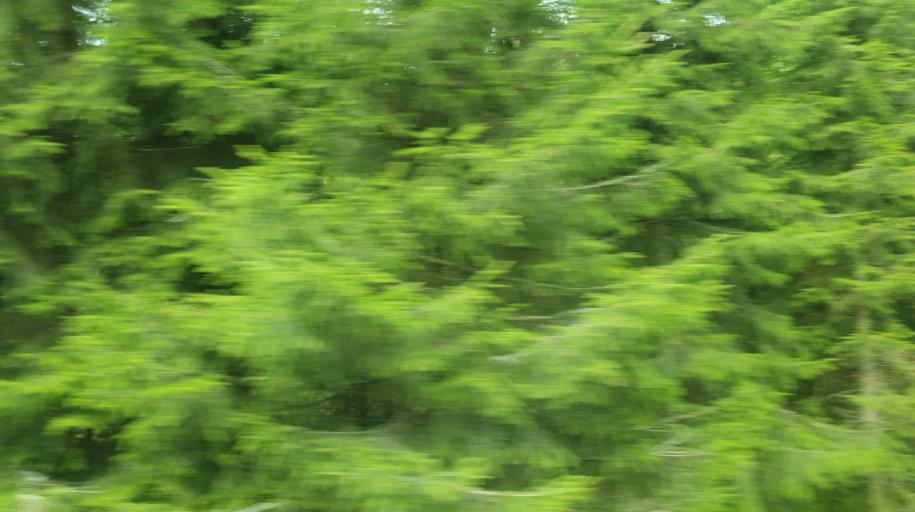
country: NO
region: Nord-Trondelag
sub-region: Levanger
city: Skogn
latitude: 63.6200
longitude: 11.2121
